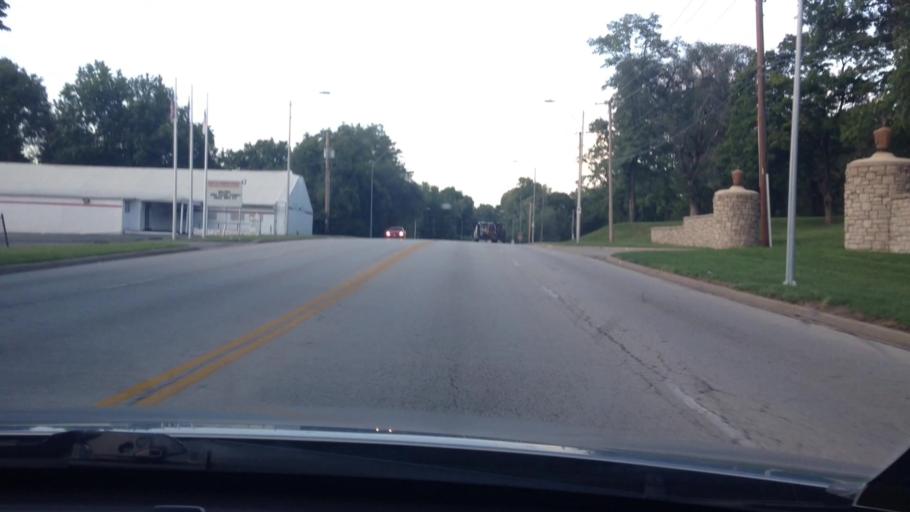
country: US
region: Missouri
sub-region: Jackson County
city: Raytown
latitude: 38.9861
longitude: -94.4831
